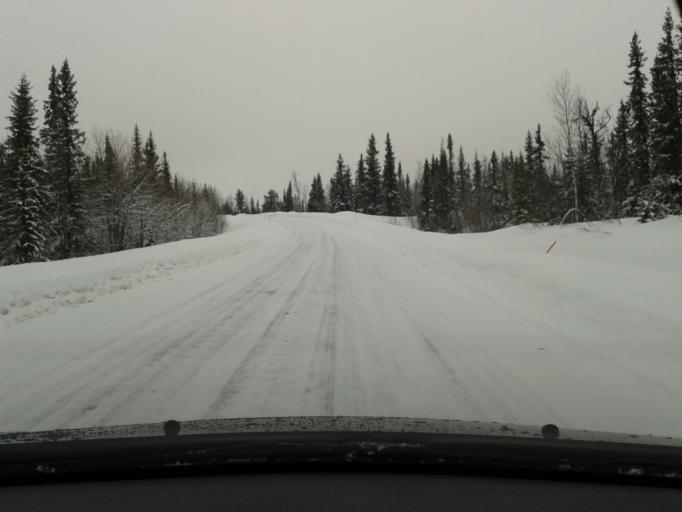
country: SE
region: Vaesterbotten
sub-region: Vilhelmina Kommun
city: Sjoberg
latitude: 65.1541
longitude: 15.8617
